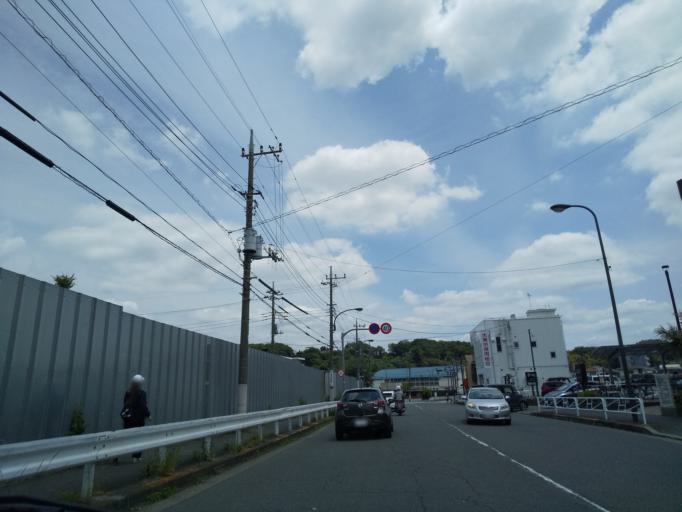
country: JP
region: Tokyo
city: Hachioji
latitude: 35.6731
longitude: 139.3251
